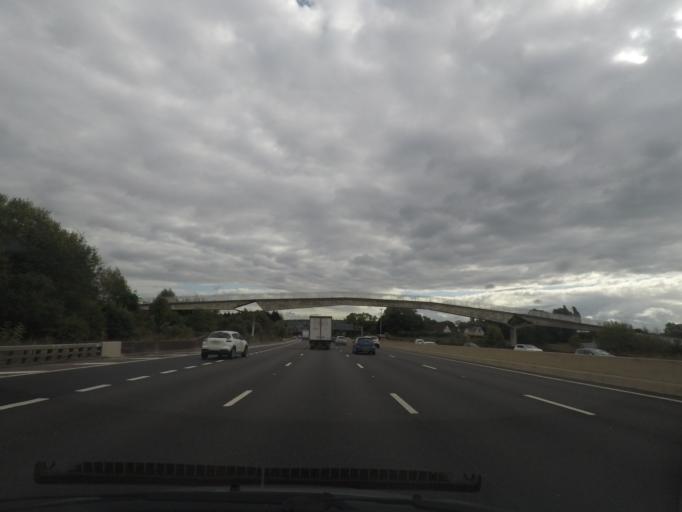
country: GB
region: England
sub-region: Sheffield
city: Chapletown
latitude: 53.4505
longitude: -1.4447
